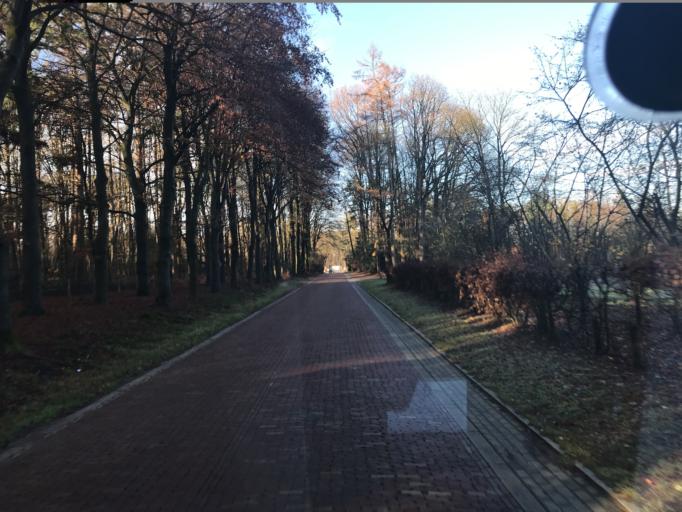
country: NL
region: Gelderland
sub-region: Gemeente Apeldoorn
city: Uddel
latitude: 52.1991
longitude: 5.8399
